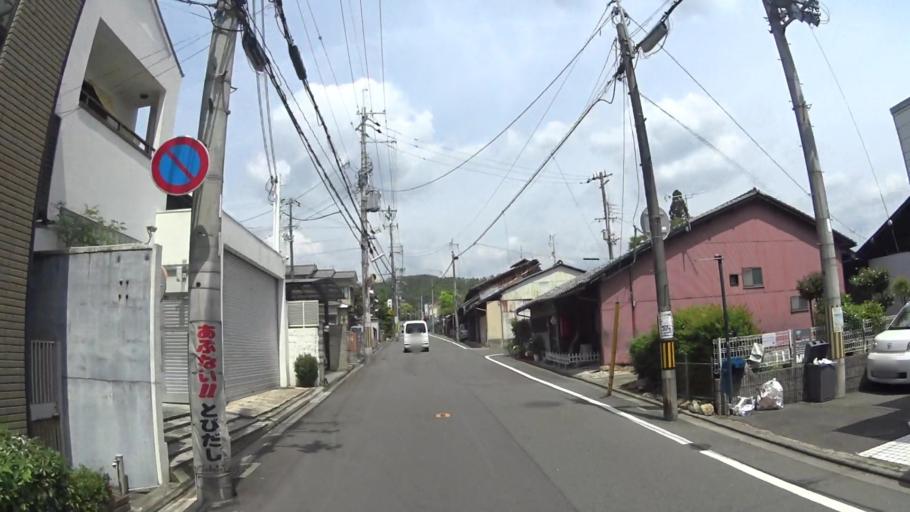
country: JP
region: Kyoto
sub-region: Kyoto-shi
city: Kamigyo-ku
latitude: 35.0517
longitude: 135.7338
